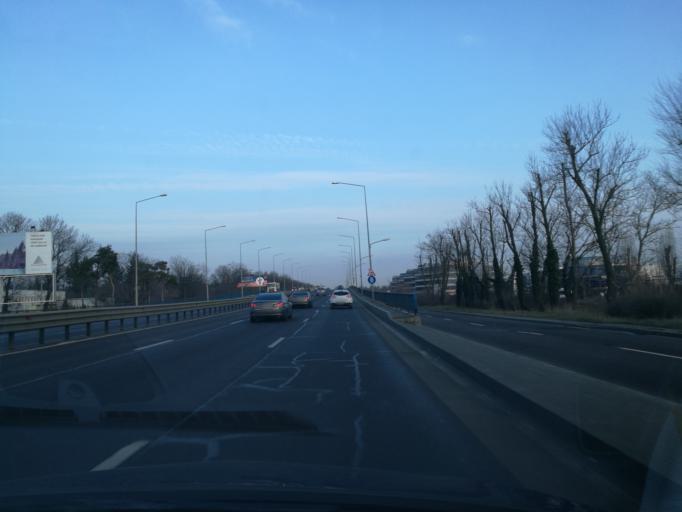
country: RO
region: Ilfov
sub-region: Comuna Otopeni
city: Otopeni
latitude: 44.5113
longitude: 26.0814
